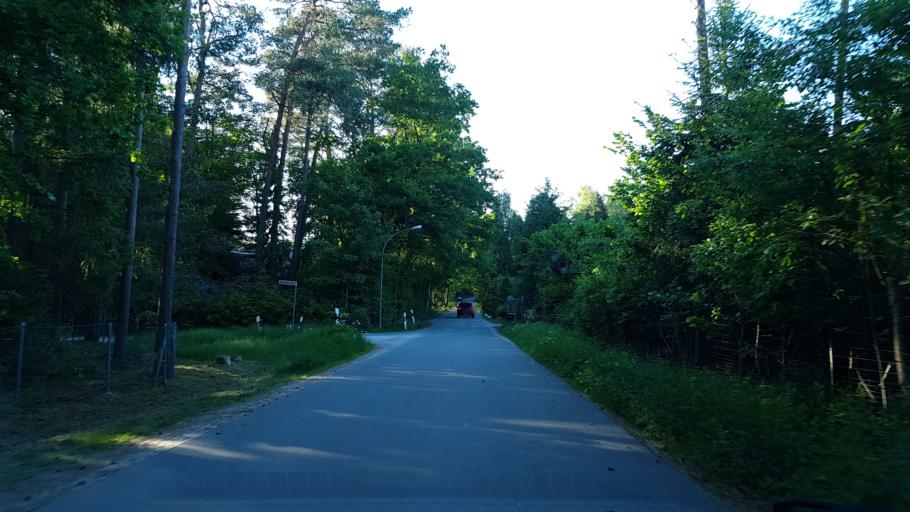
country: DE
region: Lower Saxony
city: Stelle
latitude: 53.3556
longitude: 10.1049
